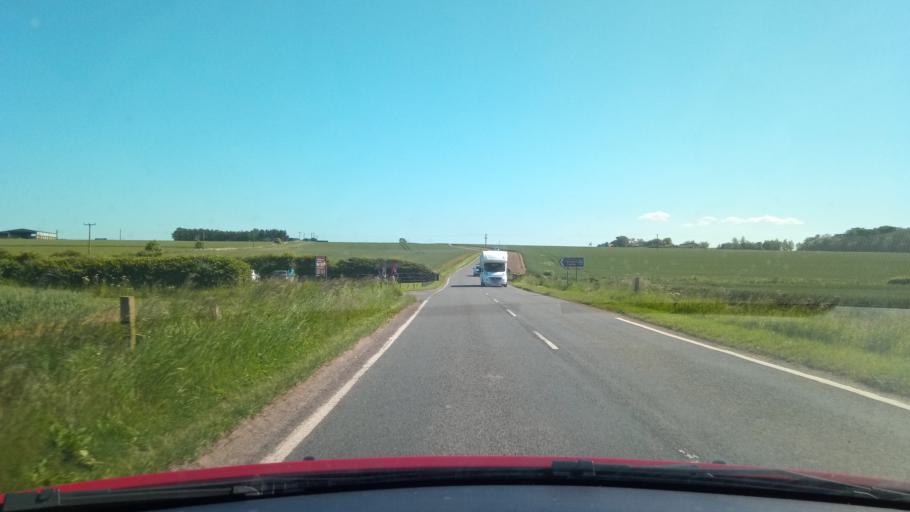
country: GB
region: Scotland
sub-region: East Lothian
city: North Berwick
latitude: 56.0545
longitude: -2.6592
